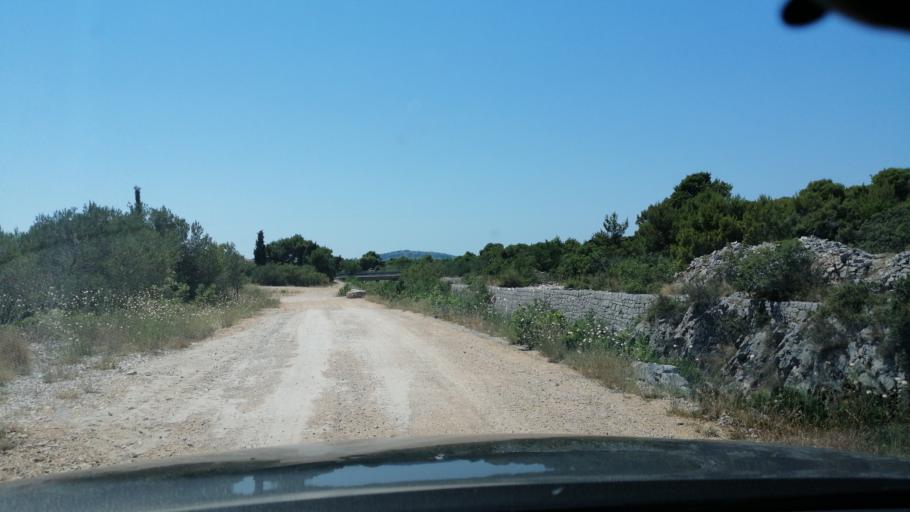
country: HR
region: Sibensko-Kniniska
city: Murter
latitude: 43.8464
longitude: 15.6264
